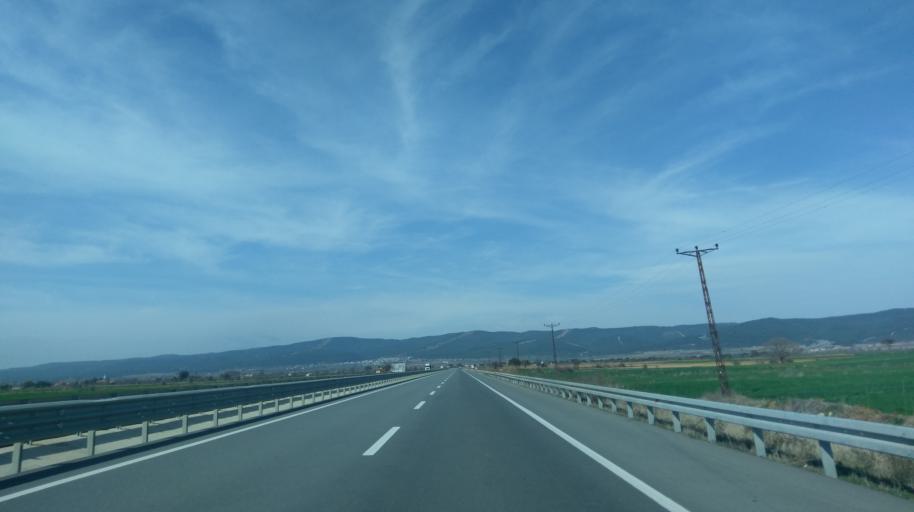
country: TR
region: Canakkale
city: Evrese
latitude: 40.6601
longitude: 26.8141
